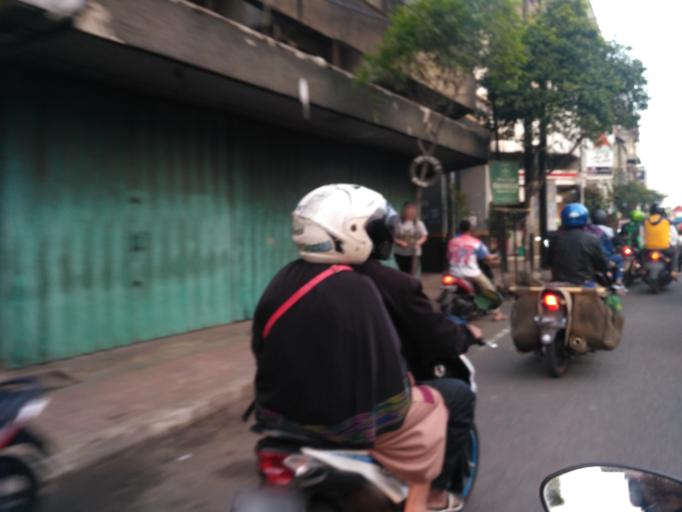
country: ID
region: East Java
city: Malang
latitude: -7.9958
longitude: 112.6330
